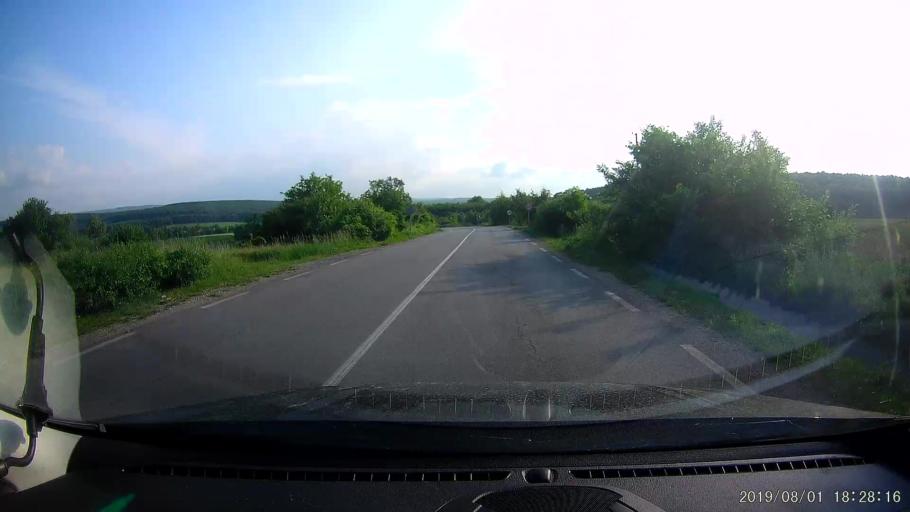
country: BG
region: Shumen
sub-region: Obshtina Venets
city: Venets
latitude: 43.5770
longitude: 26.9671
